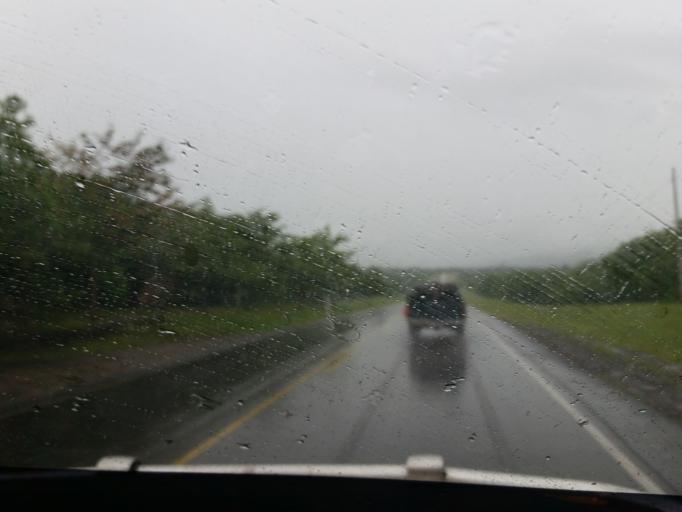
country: NI
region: Matagalpa
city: Ciudad Dario
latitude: 12.7248
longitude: -86.1056
